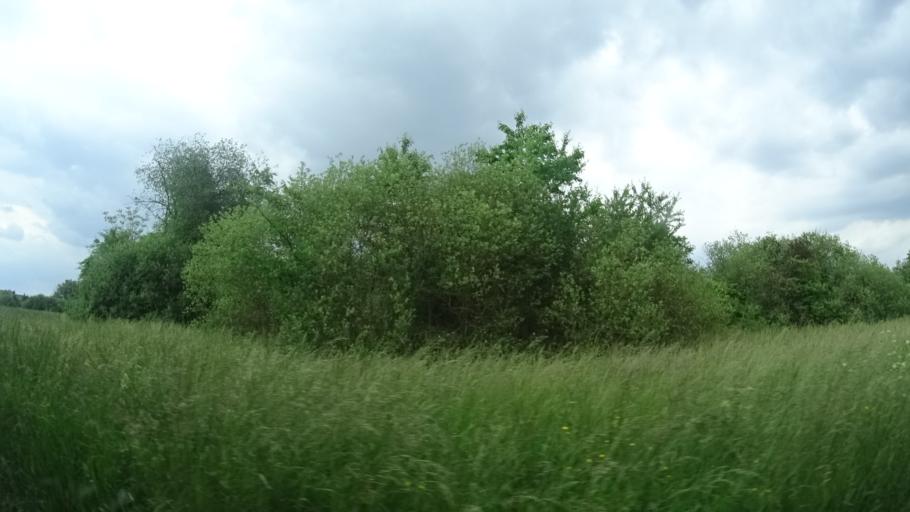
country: DE
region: Rheinland-Pfalz
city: Schifferstadt
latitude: 49.3782
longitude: 8.3624
